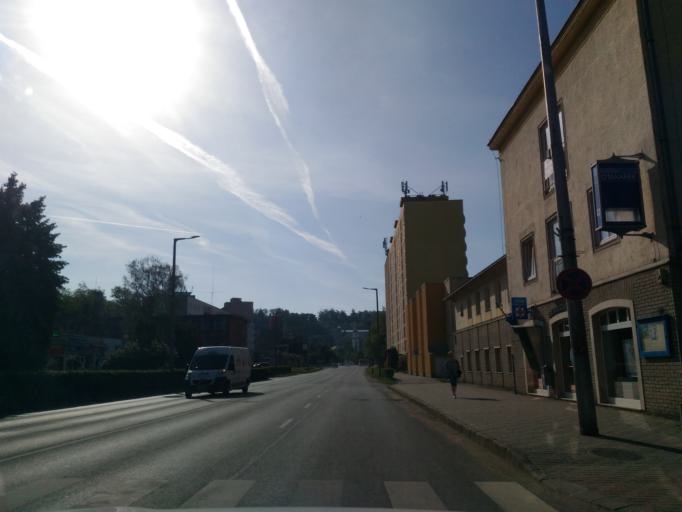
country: HU
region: Baranya
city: Komlo
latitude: 46.1909
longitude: 18.2626
